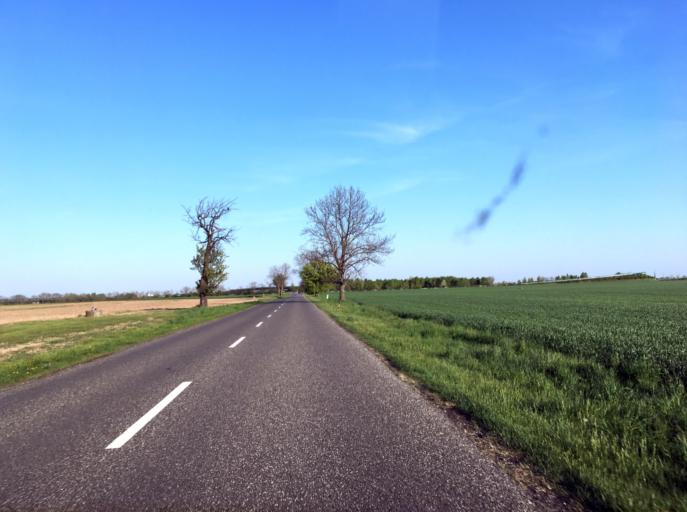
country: AT
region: Burgenland
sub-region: Politischer Bezirk Neusiedl am See
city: Kittsee
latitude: 48.0754
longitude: 17.0863
